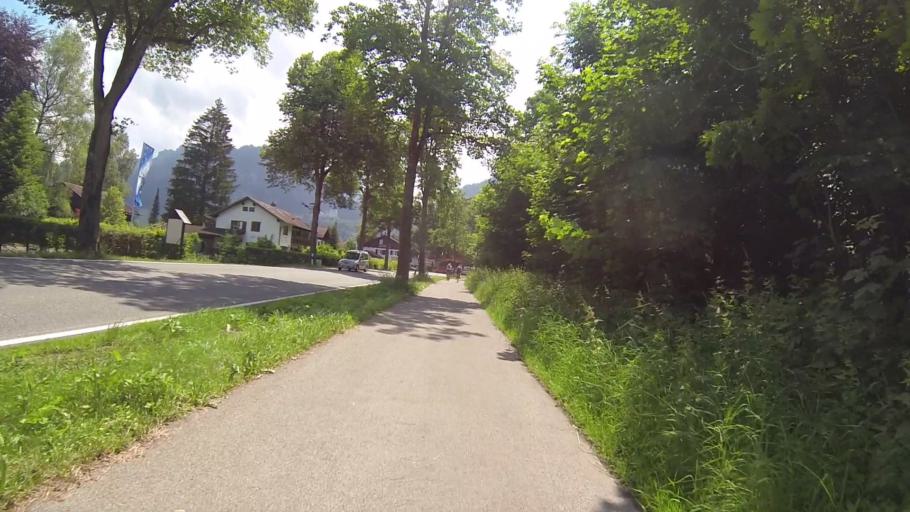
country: DE
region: Bavaria
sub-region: Swabia
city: Schwangau
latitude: 47.5654
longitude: 10.7257
